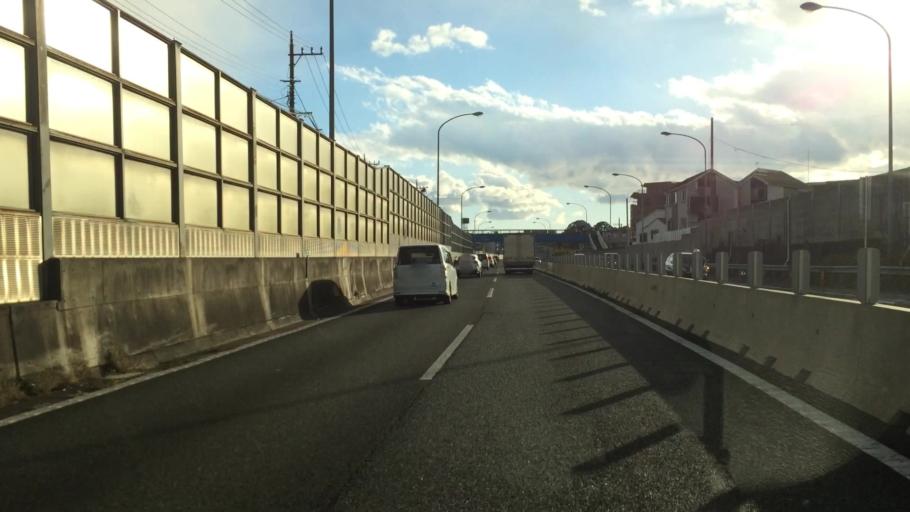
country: JP
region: Kanagawa
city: Fujisawa
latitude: 35.4213
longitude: 139.5386
